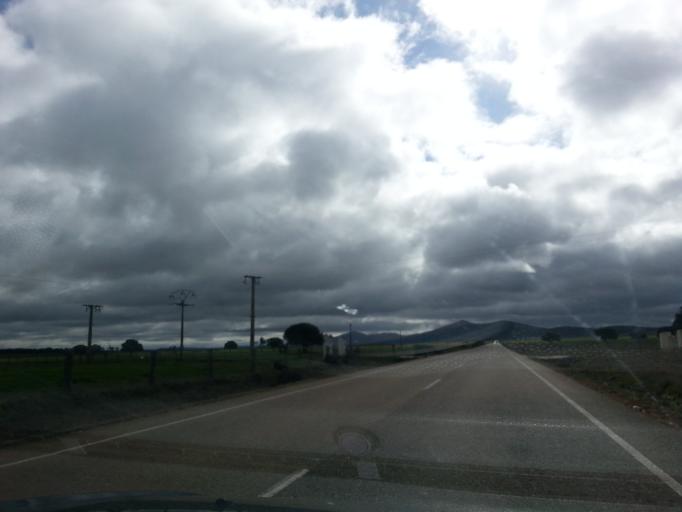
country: ES
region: Castille and Leon
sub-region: Provincia de Salamanca
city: Tamames
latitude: 40.6796
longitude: -6.1281
